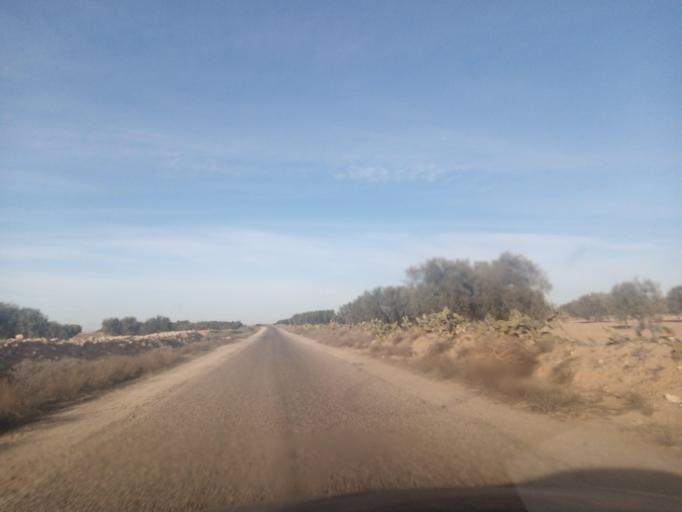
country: TN
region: Safaqis
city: Bi'r `Ali Bin Khalifah
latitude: 34.8532
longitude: 10.1625
